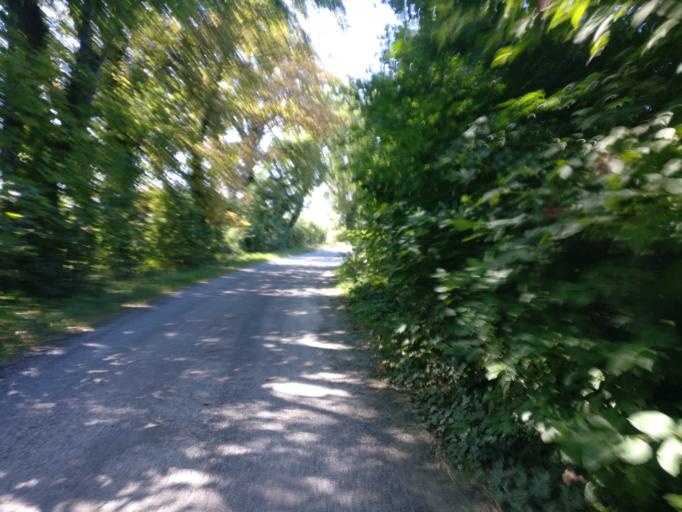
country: AT
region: Lower Austria
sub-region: Politischer Bezirk Baden
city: Pottendorf
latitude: 47.9094
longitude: 16.3541
